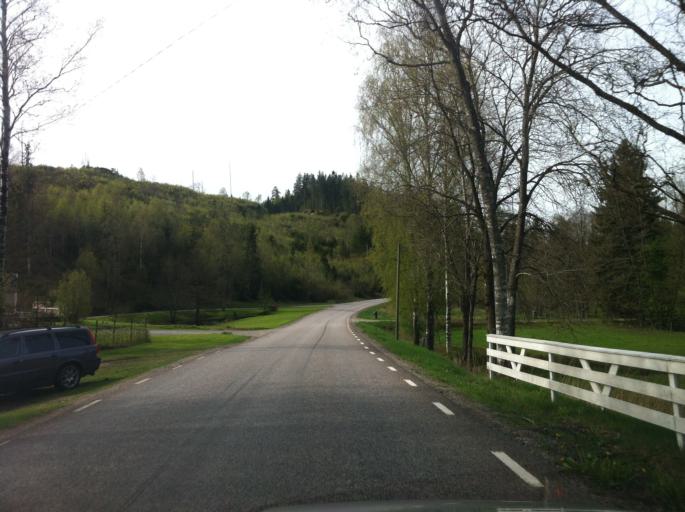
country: SE
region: Vaestra Goetaland
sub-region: Bollebygds Kommun
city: Bollebygd
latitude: 57.5756
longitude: 12.5607
